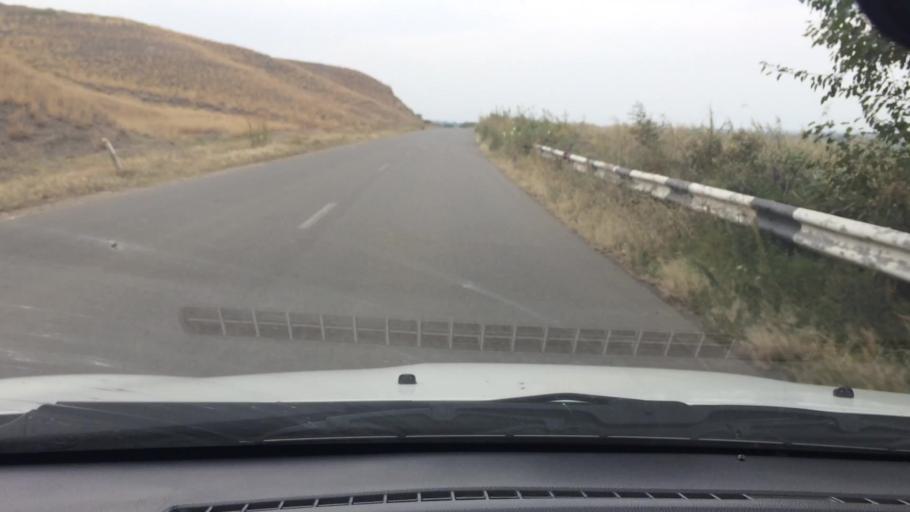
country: AM
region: Tavush
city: Berdavan
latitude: 41.3400
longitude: 44.9964
